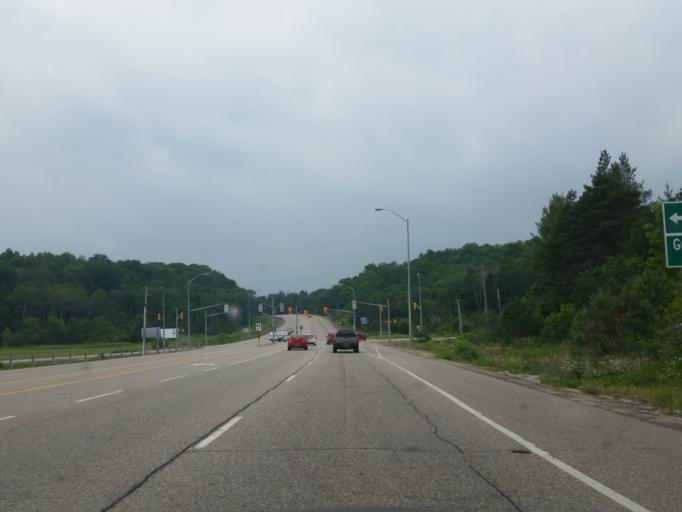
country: CA
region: Ontario
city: Huntsville
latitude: 45.3443
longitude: -79.1589
